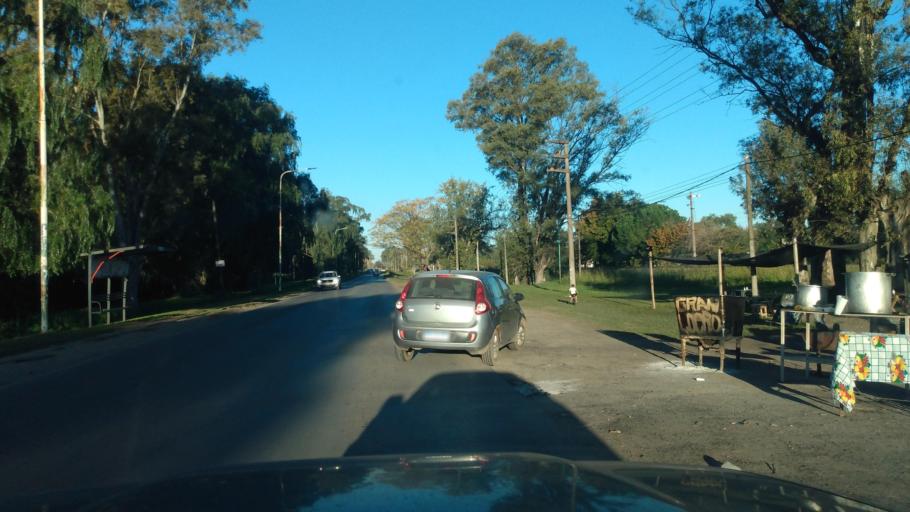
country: AR
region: Buenos Aires
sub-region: Partido de General Rodriguez
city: General Rodriguez
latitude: -34.6339
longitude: -58.8482
